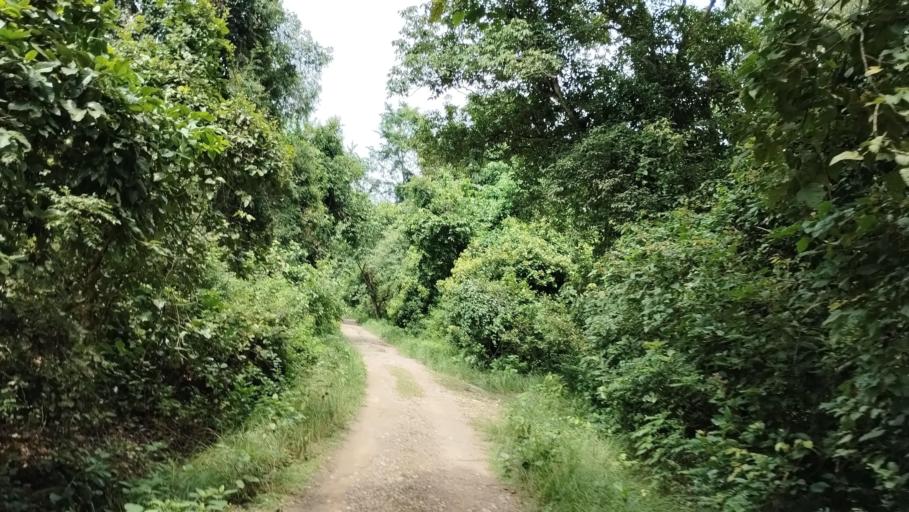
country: NP
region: Far Western
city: Tikapur
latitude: 28.4553
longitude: 81.2422
